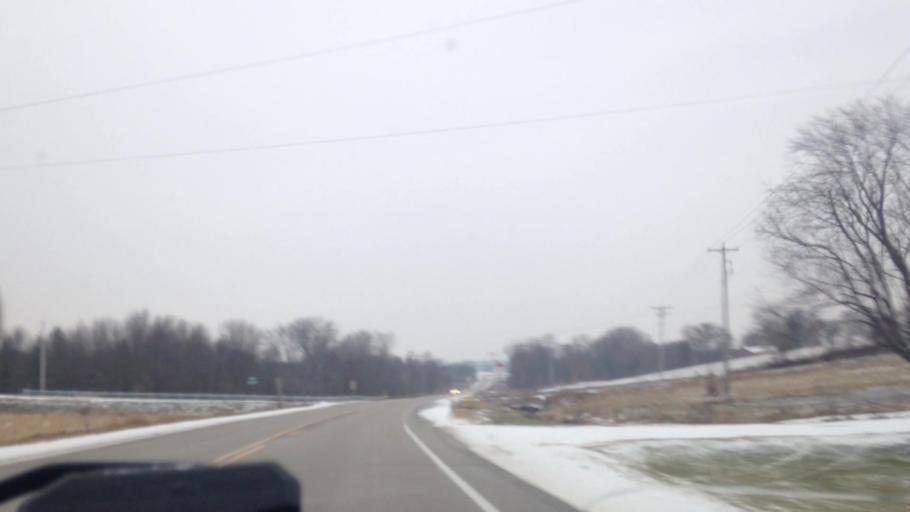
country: US
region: Wisconsin
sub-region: Dodge County
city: Hustisford
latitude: 43.3419
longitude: -88.5135
